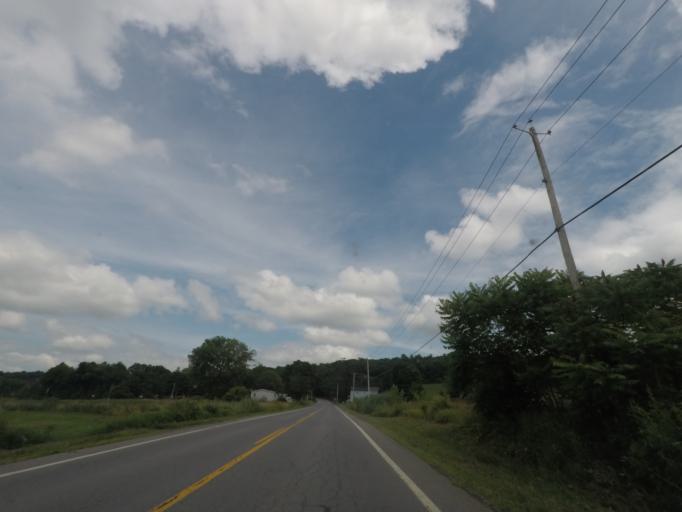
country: US
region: New York
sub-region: Saratoga County
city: Stillwater
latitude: 43.0236
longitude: -73.6917
